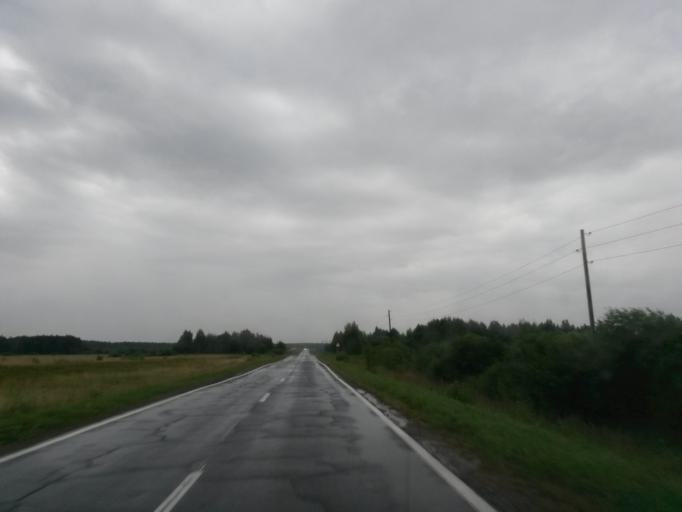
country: RU
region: Jaroslavl
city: Tutayev
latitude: 57.9495
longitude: 39.4532
